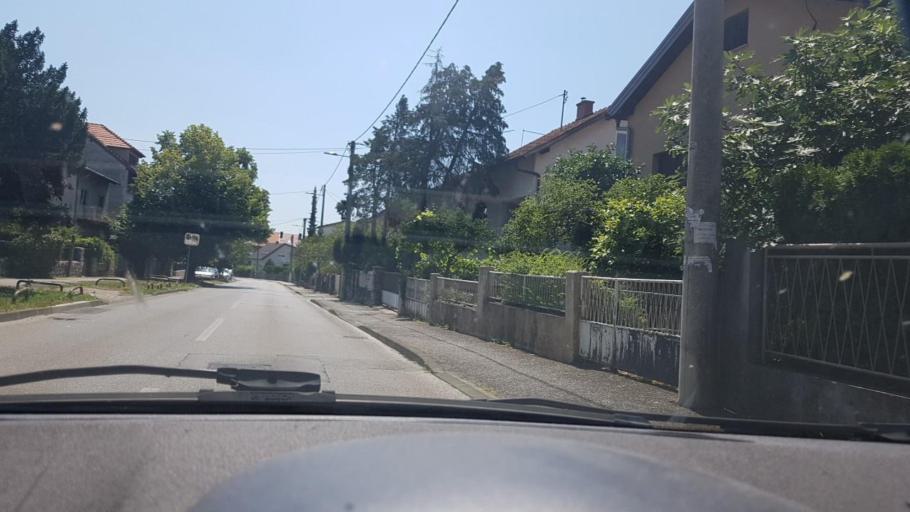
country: HR
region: Grad Zagreb
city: Zagreb
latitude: 45.8316
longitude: 15.9926
